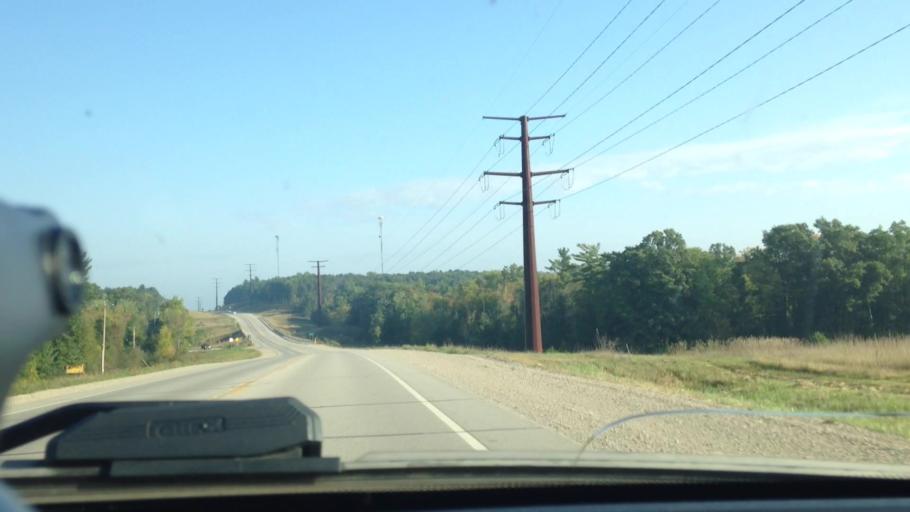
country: US
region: Wisconsin
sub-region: Marinette County
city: Peshtigo
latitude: 45.2053
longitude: -87.9942
